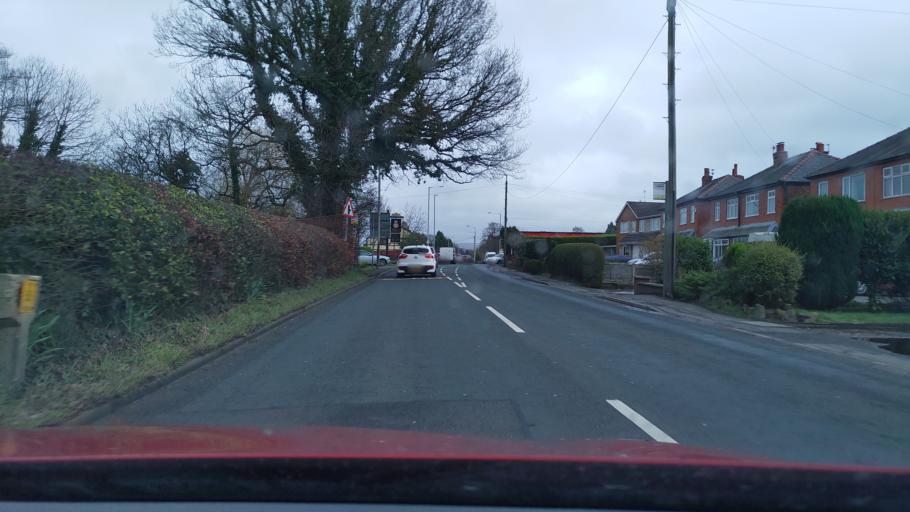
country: GB
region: England
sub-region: Lancashire
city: Croston
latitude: 53.6632
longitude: -2.7402
